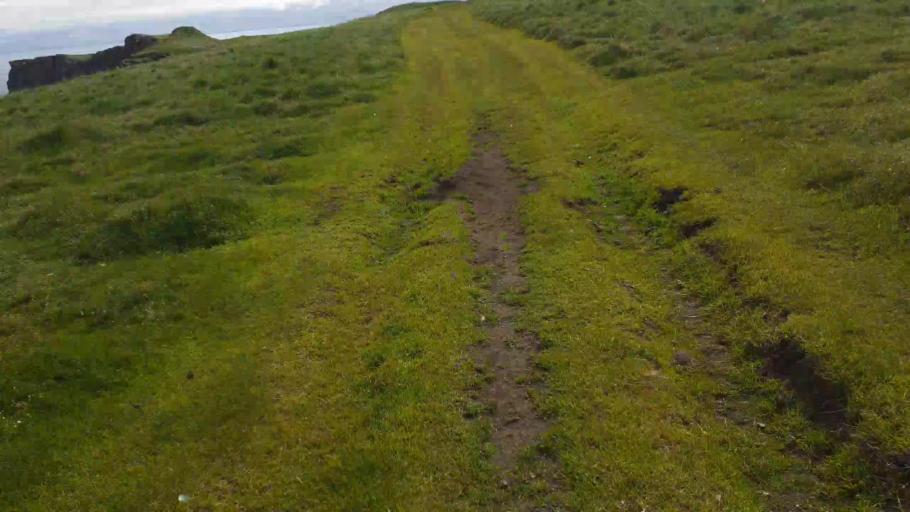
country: IS
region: Northeast
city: Dalvik
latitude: 66.5501
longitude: -17.9925
